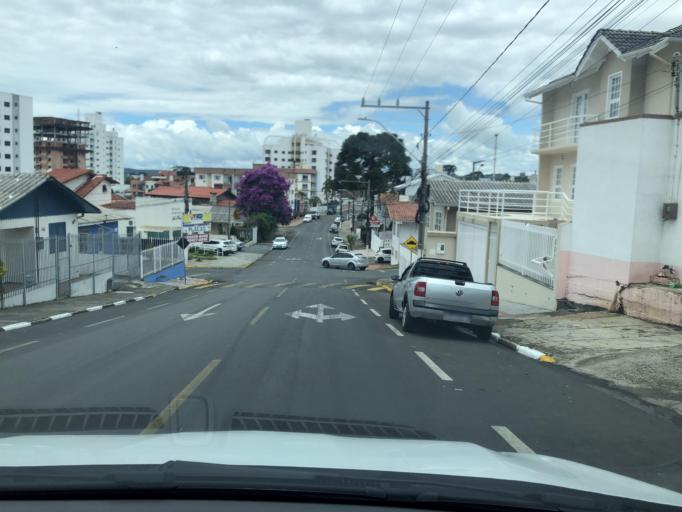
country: BR
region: Santa Catarina
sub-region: Lages
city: Lages
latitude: -27.8216
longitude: -50.3271
